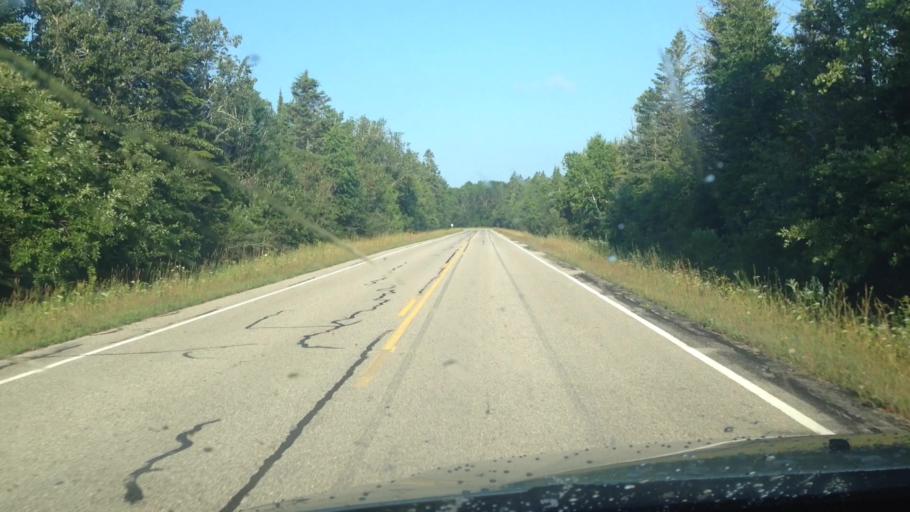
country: US
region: Michigan
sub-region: Mackinac County
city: Saint Ignace
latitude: 45.8930
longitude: -84.7809
